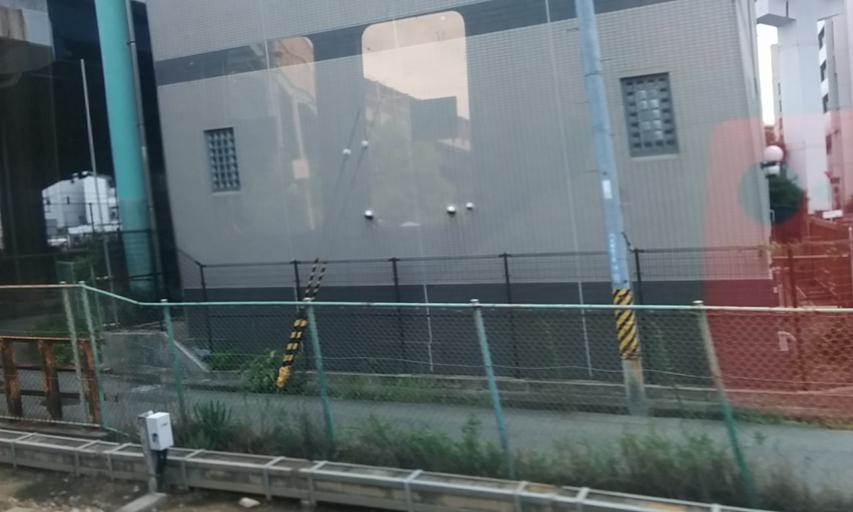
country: JP
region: Osaka
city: Takatsuki
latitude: 34.8546
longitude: 135.5813
